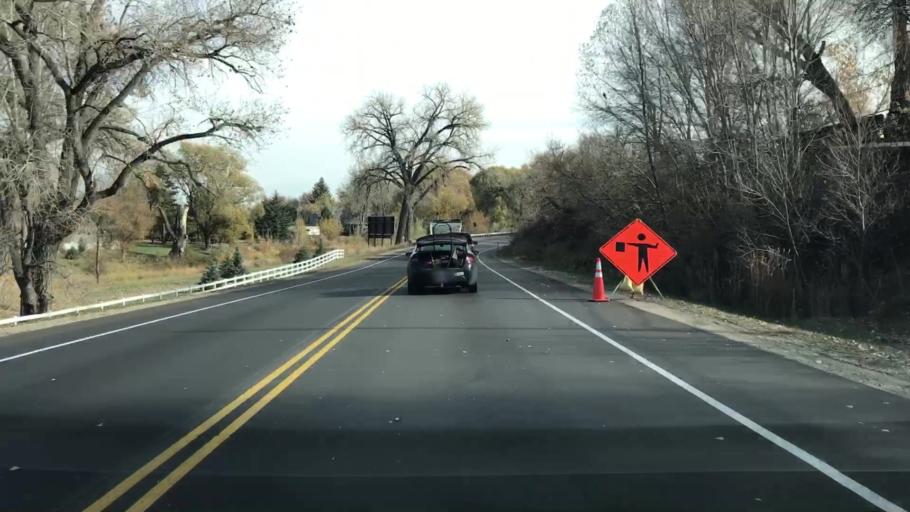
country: US
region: Colorado
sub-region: Larimer County
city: Loveland
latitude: 40.4154
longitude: -105.1716
